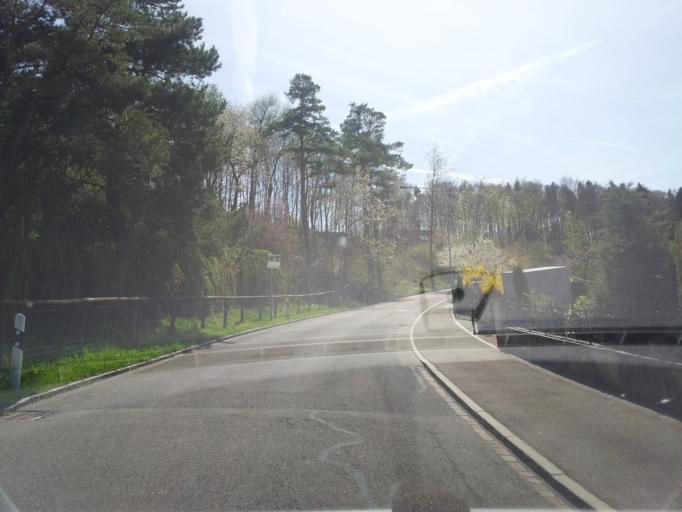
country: CH
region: Zurich
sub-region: Bezirk Dielsdorf
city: Otelfingen
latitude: 47.4429
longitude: 8.3870
